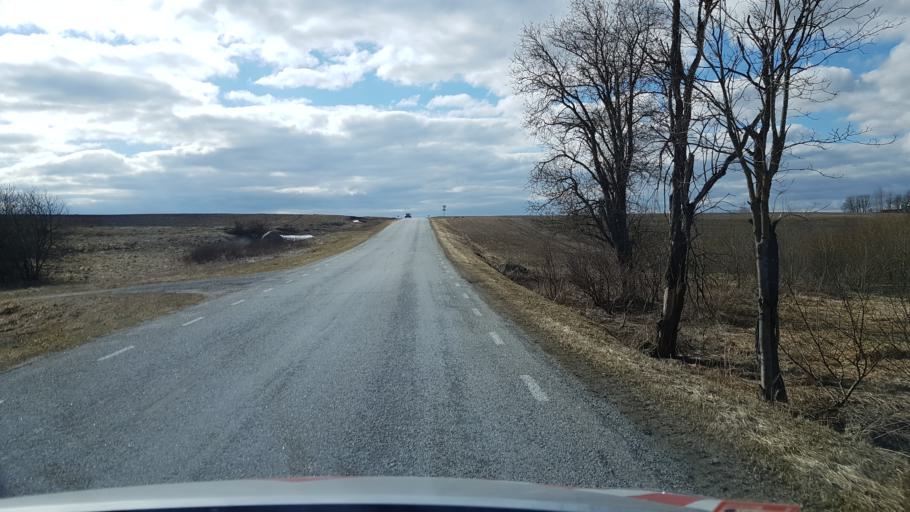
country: EE
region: Laeaene-Virumaa
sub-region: Kadrina vald
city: Kadrina
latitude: 59.2898
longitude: 26.1820
